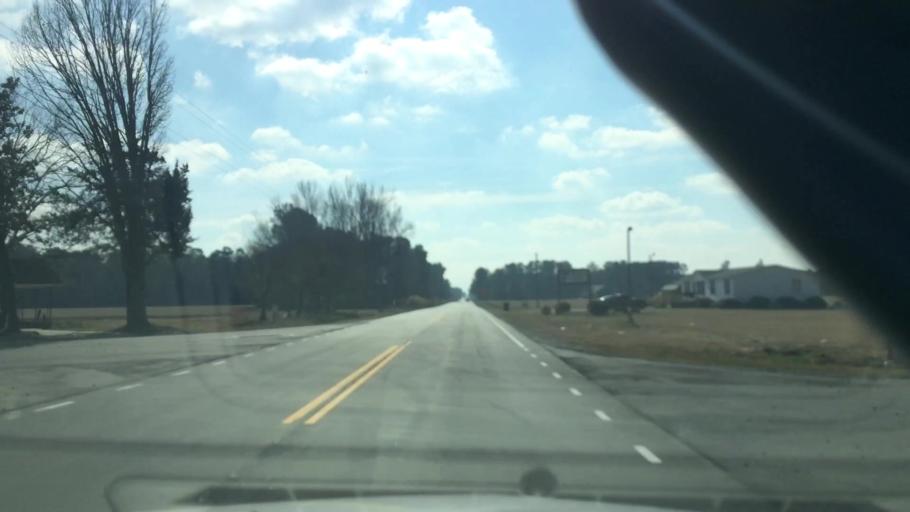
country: US
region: North Carolina
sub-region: Duplin County
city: Beulaville
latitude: 35.0296
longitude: -77.7482
